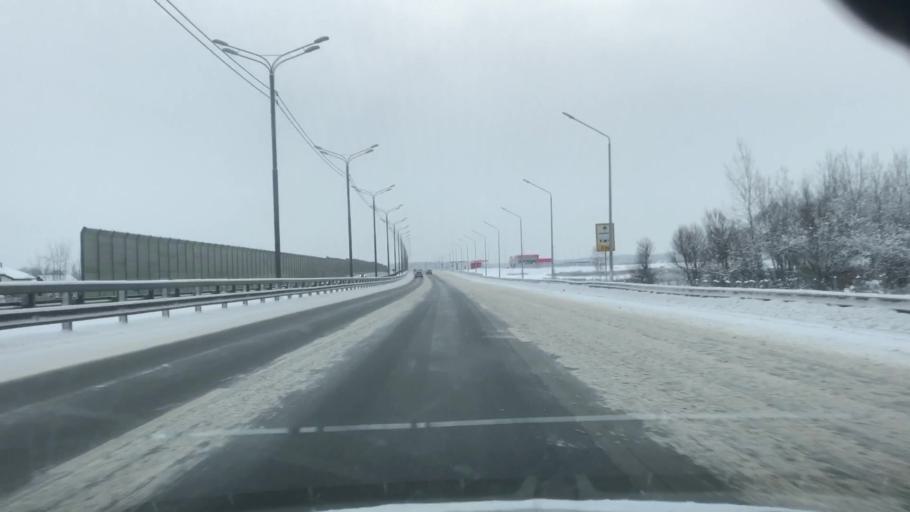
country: RU
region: Moskovskaya
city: Barybino
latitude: 55.1970
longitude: 37.8904
